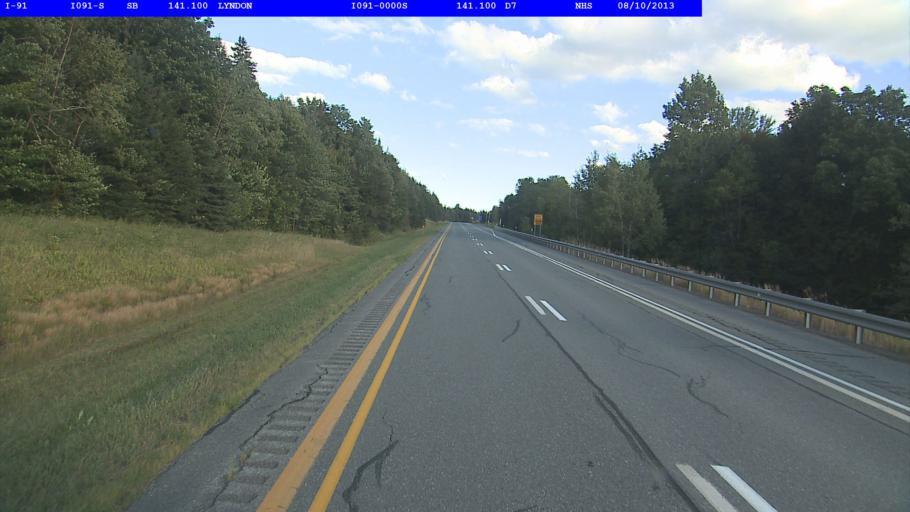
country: US
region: Vermont
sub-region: Caledonia County
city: Lyndonville
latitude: 44.5681
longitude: -72.0368
